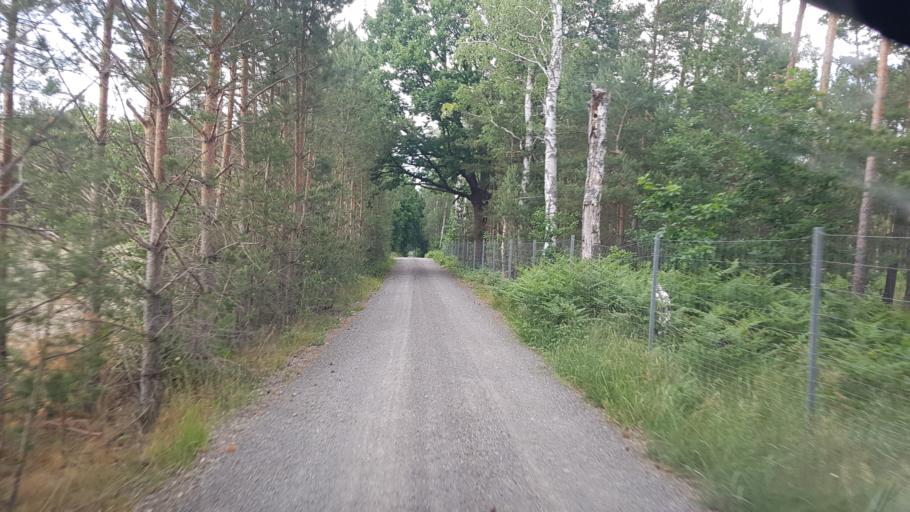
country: DE
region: Brandenburg
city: Plessa
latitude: 51.5433
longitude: 13.6406
